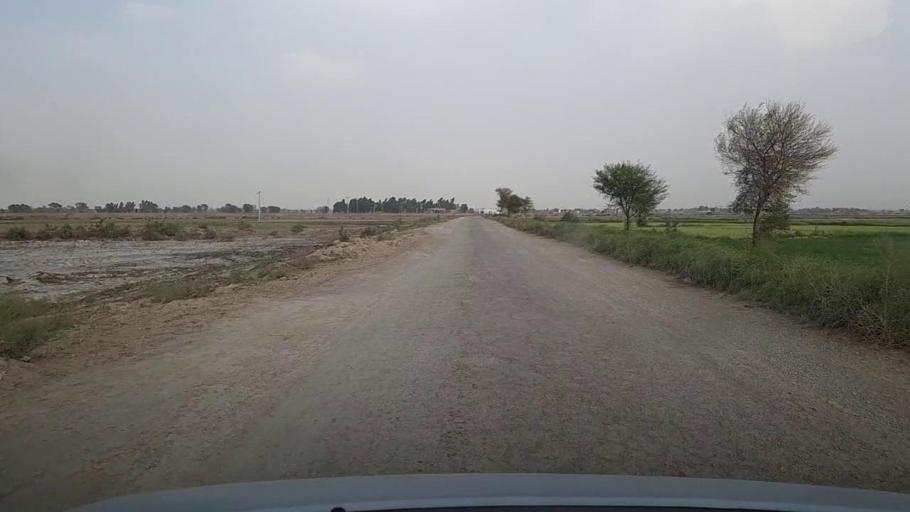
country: PK
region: Sindh
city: Dadu
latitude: 26.8133
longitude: 67.7748
